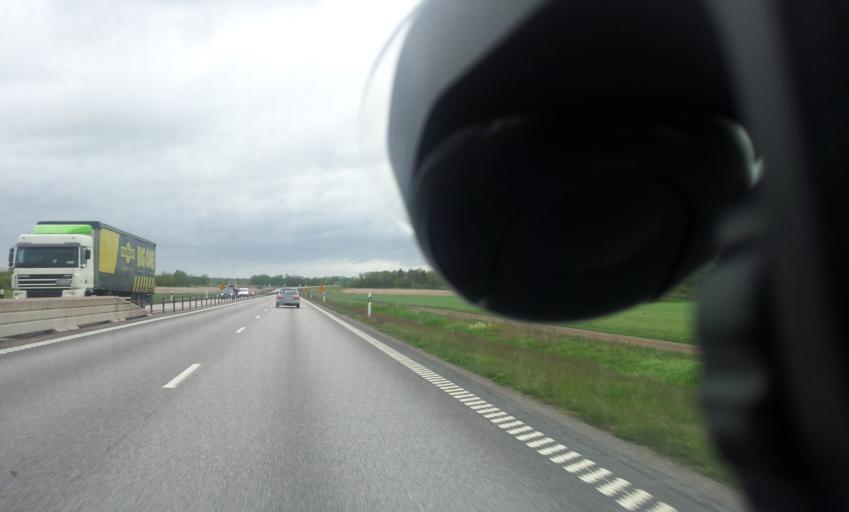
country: SE
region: Kalmar
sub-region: Kalmar Kommun
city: Ljungbyholm
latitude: 56.6030
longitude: 16.1324
